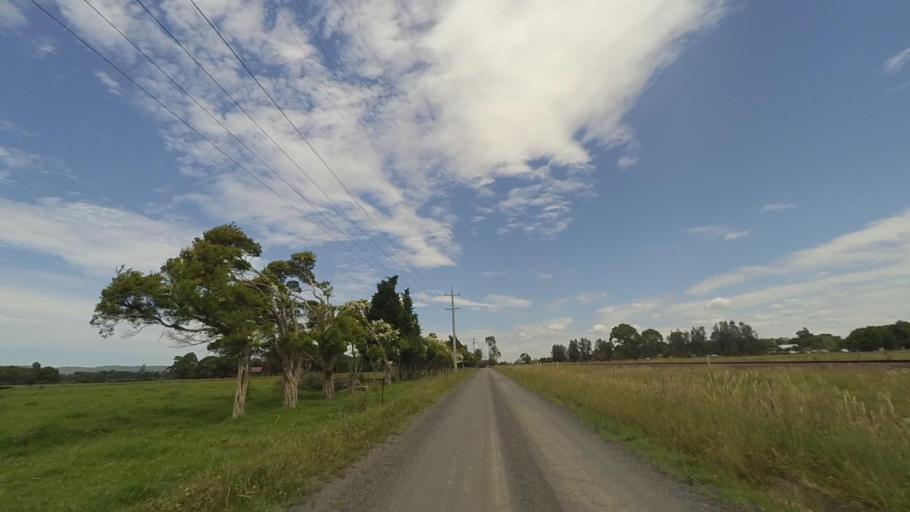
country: AU
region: New South Wales
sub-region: Shoalhaven Shire
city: Berry
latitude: -34.7927
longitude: 150.6778
